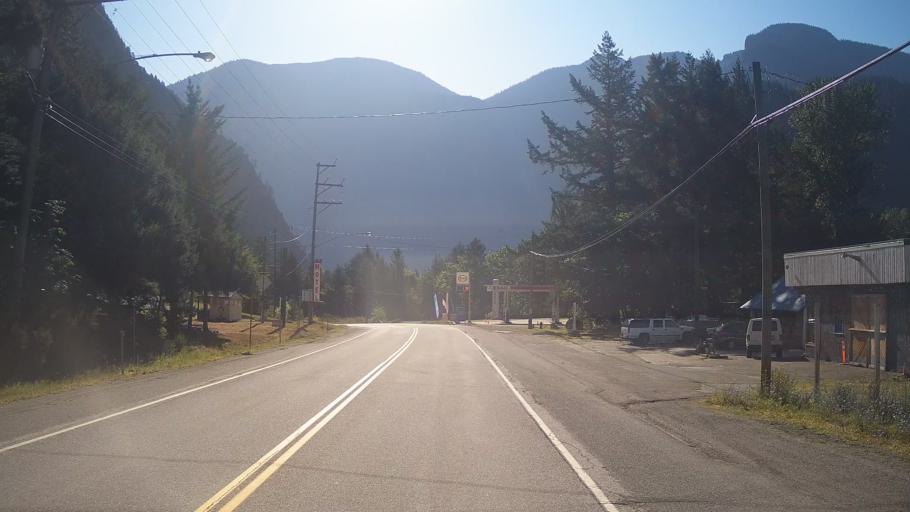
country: CA
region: British Columbia
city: Hope
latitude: 49.5630
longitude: -121.4299
